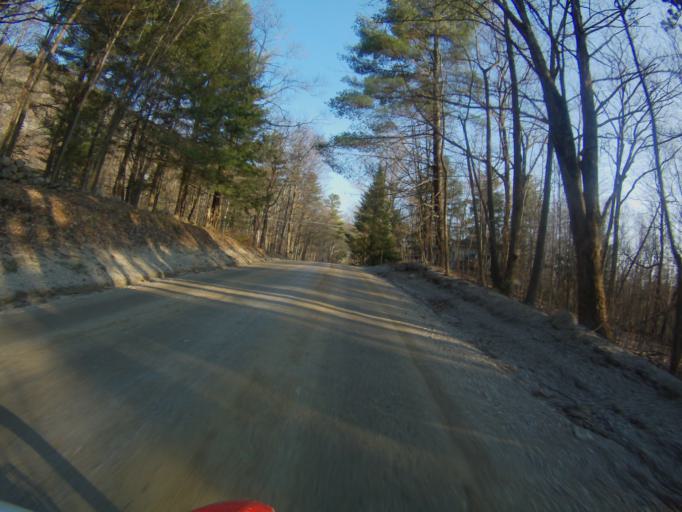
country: US
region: Vermont
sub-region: Addison County
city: Bristol
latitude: 44.1164
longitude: -73.0788
